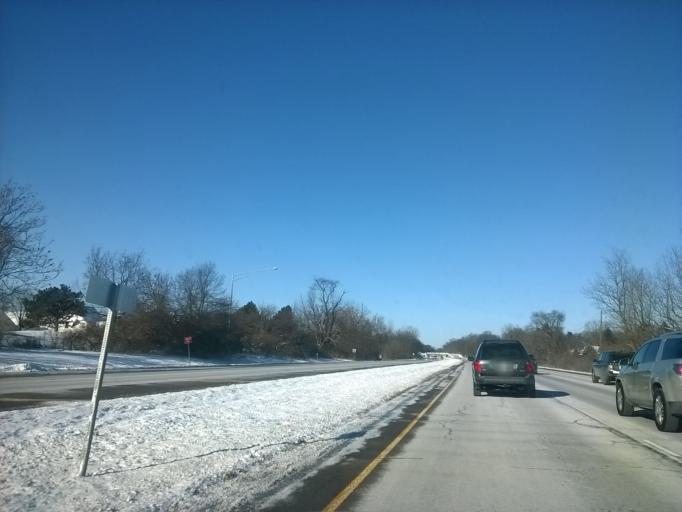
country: US
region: Indiana
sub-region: Hamilton County
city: Carmel
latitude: 39.9341
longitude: -86.1122
